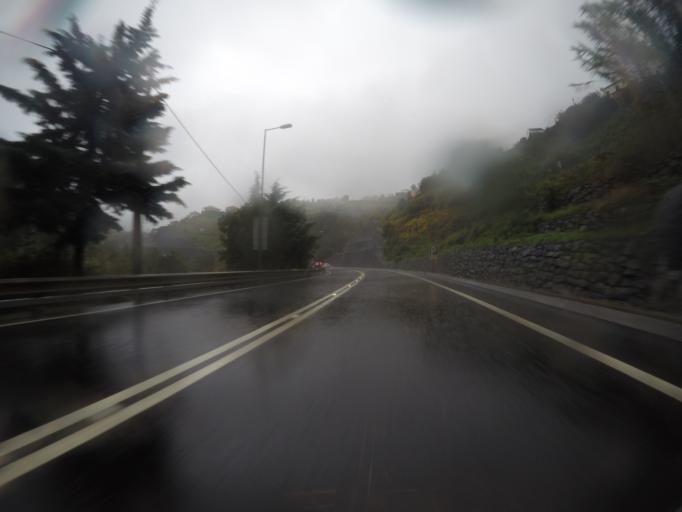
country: PT
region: Madeira
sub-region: Santana
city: Santana
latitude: 32.7649
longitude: -16.8358
